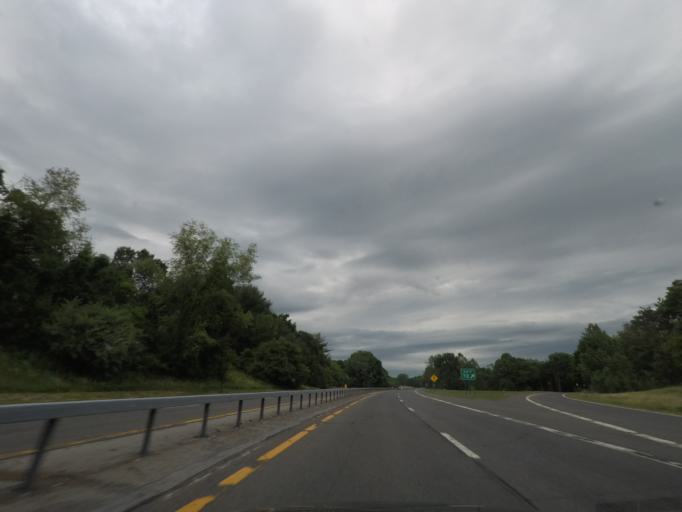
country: US
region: New York
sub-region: Dutchess County
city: Pine Plains
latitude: 42.0141
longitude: -73.7381
